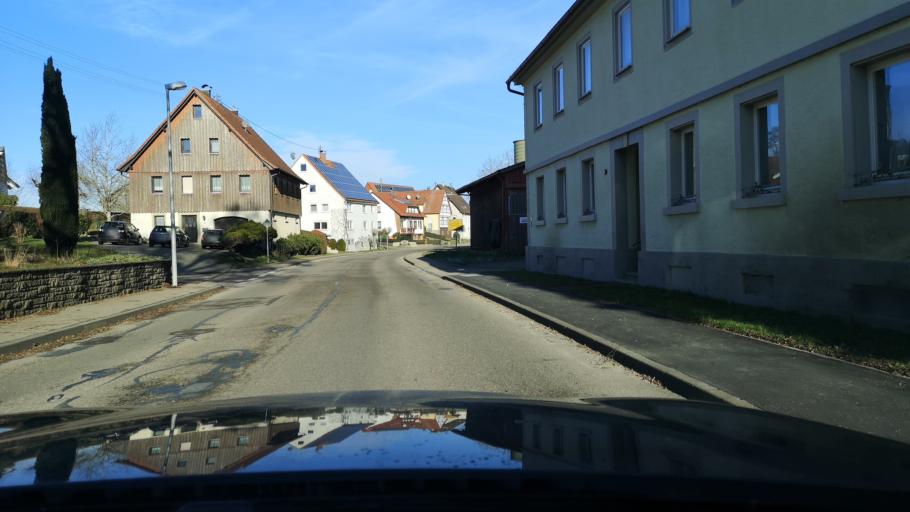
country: DE
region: Baden-Wuerttemberg
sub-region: Regierungsbezirk Stuttgart
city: Eschach
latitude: 48.8855
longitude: 9.8795
